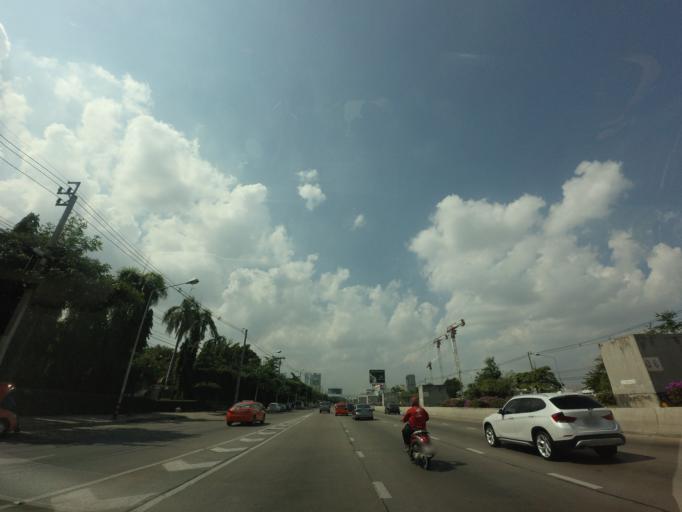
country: TH
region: Bangkok
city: Chatuchak
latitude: 13.8412
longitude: 100.5890
